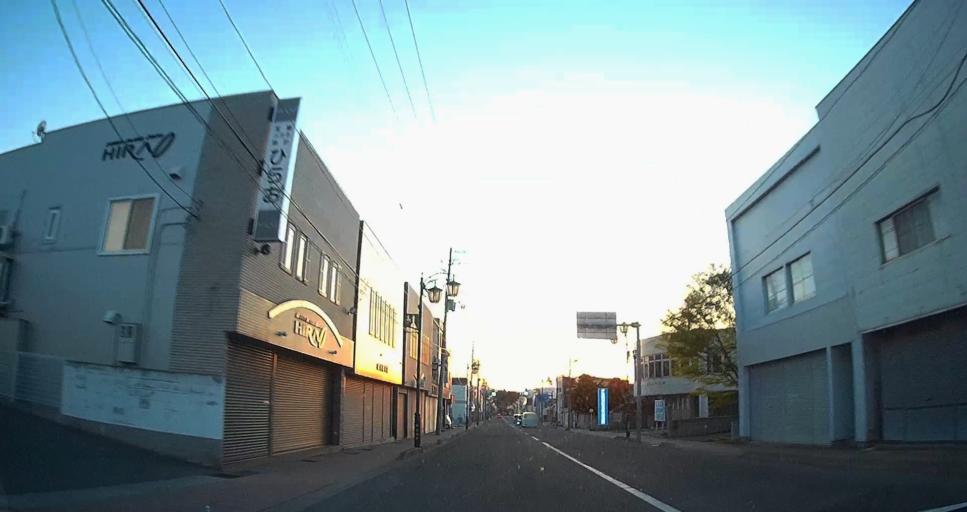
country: JP
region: Aomori
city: Misawa
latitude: 40.8666
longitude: 141.1278
